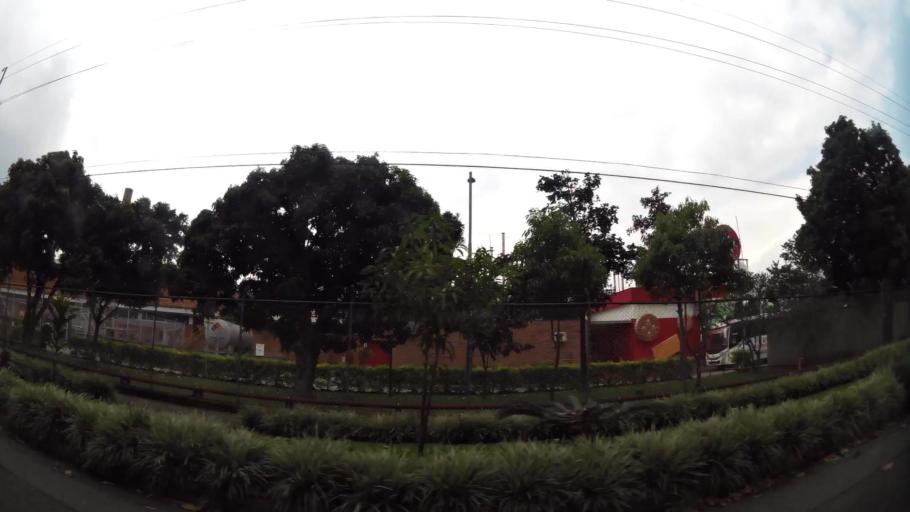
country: CO
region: Antioquia
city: Itagui
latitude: 6.2101
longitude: -75.5834
